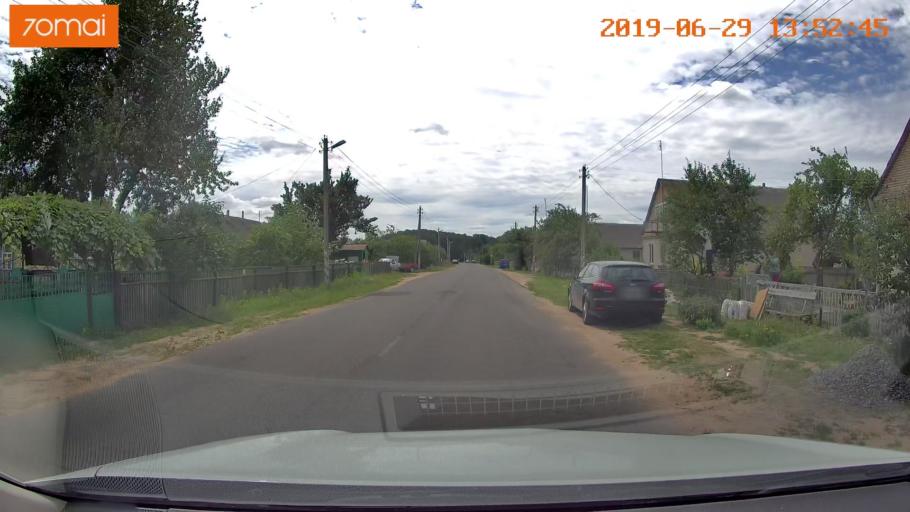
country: BY
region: Minsk
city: Slutsk
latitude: 52.9934
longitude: 27.5517
